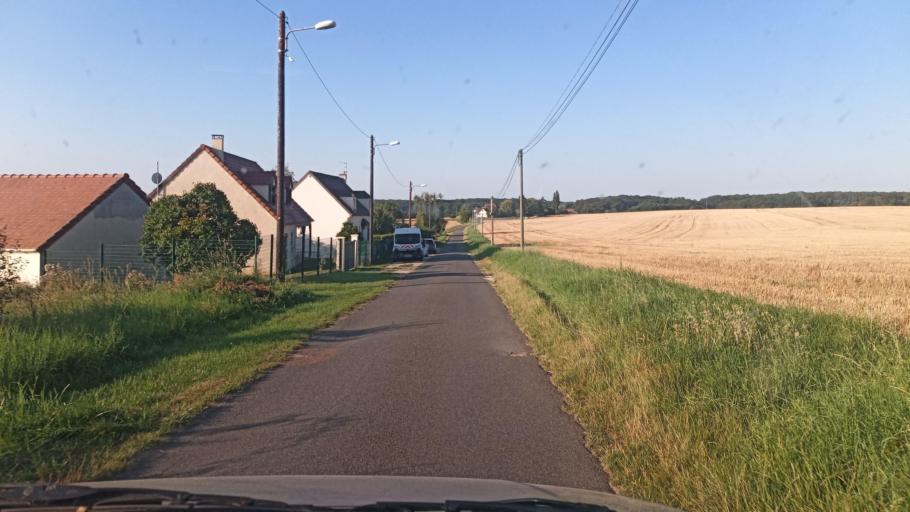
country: FR
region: Bourgogne
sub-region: Departement de l'Yonne
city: Pont-sur-Yonne
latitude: 48.2670
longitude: 3.1848
